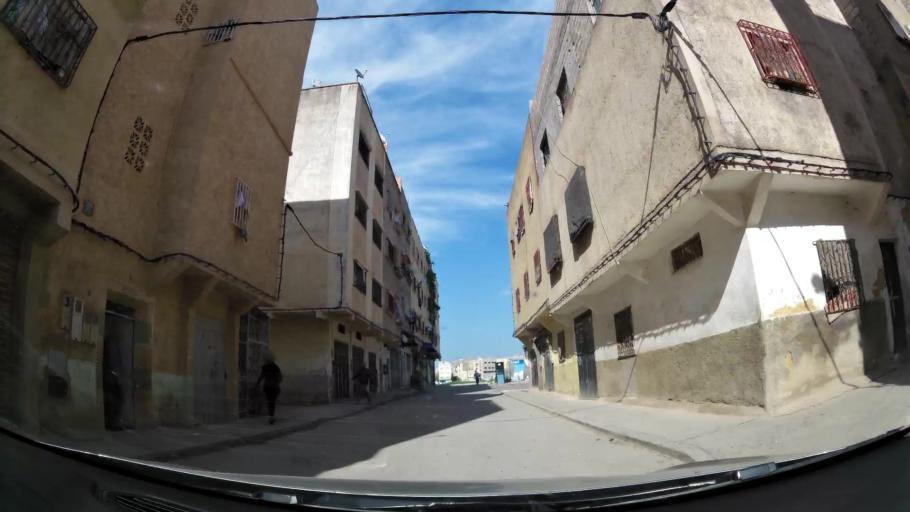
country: MA
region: Fes-Boulemane
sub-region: Fes
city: Fes
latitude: 34.0139
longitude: -5.0339
